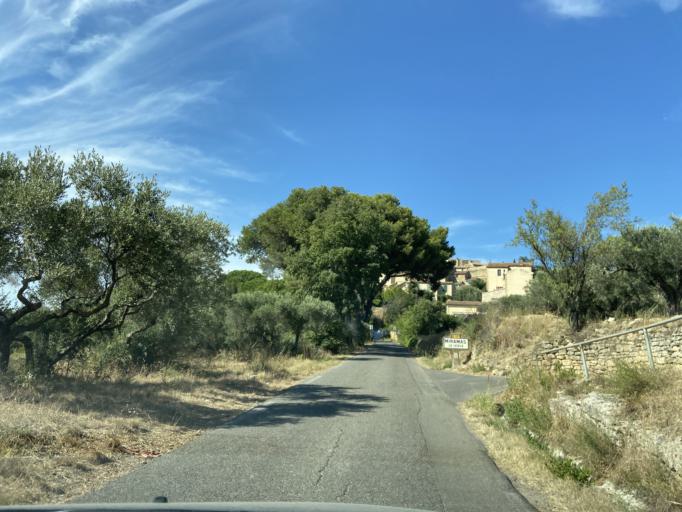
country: FR
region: Provence-Alpes-Cote d'Azur
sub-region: Departement des Bouches-du-Rhone
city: Saint-Chamas
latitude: 43.5614
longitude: 5.0235
